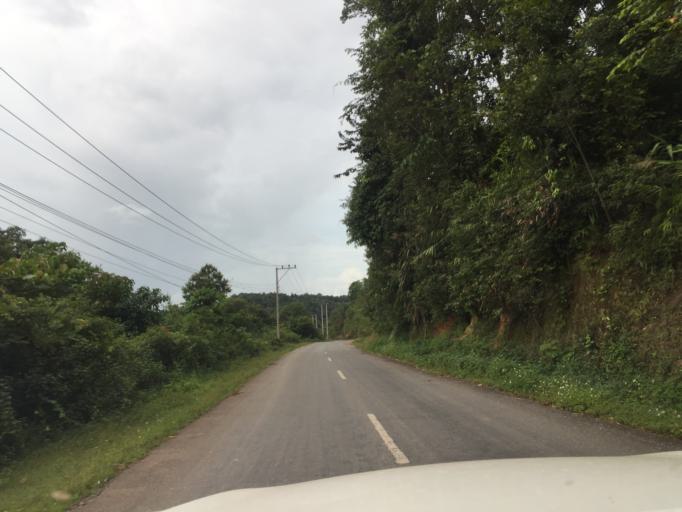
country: LA
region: Phongsali
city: Phongsali
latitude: 21.3255
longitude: 102.0515
